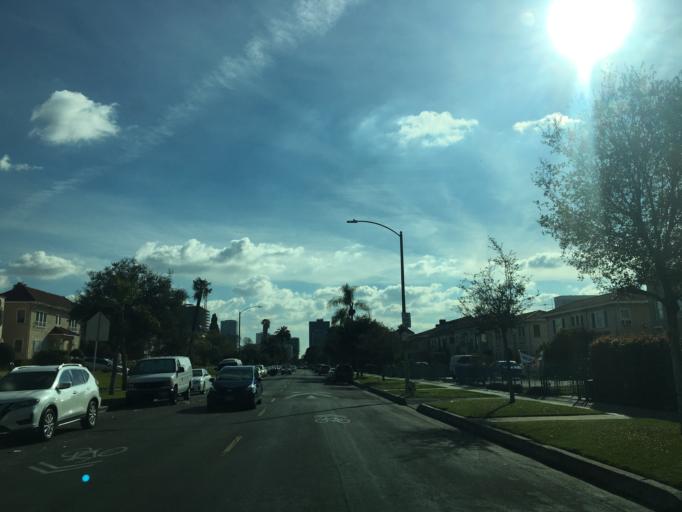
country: US
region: California
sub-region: Los Angeles County
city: Silver Lake
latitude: 34.0721
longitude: -118.2930
